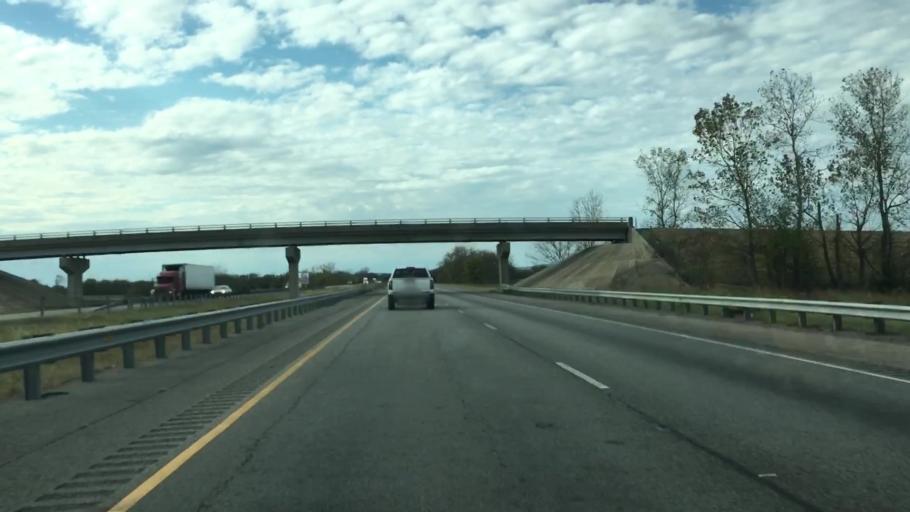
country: US
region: Arkansas
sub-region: Conway County
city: Morrilton
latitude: 35.1911
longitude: -92.7873
